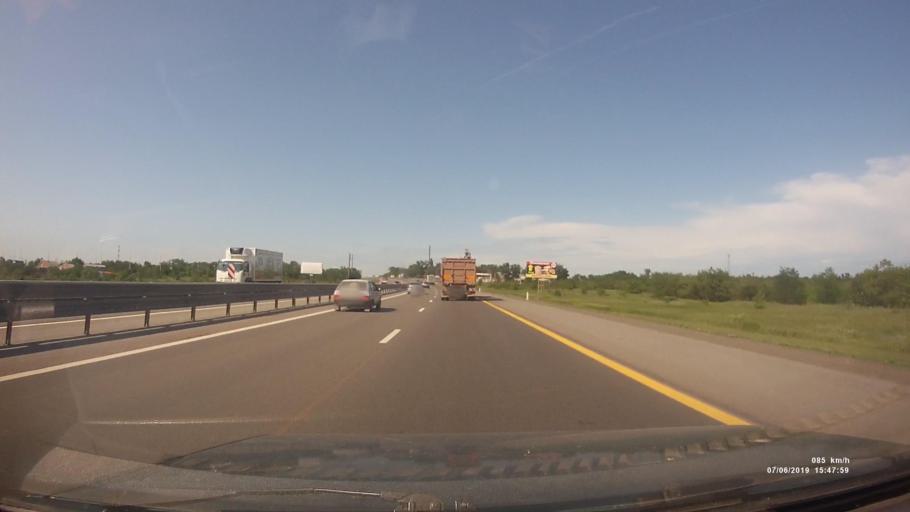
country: RU
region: Rostov
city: Ayutinskiy
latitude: 47.7692
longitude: 40.1556
